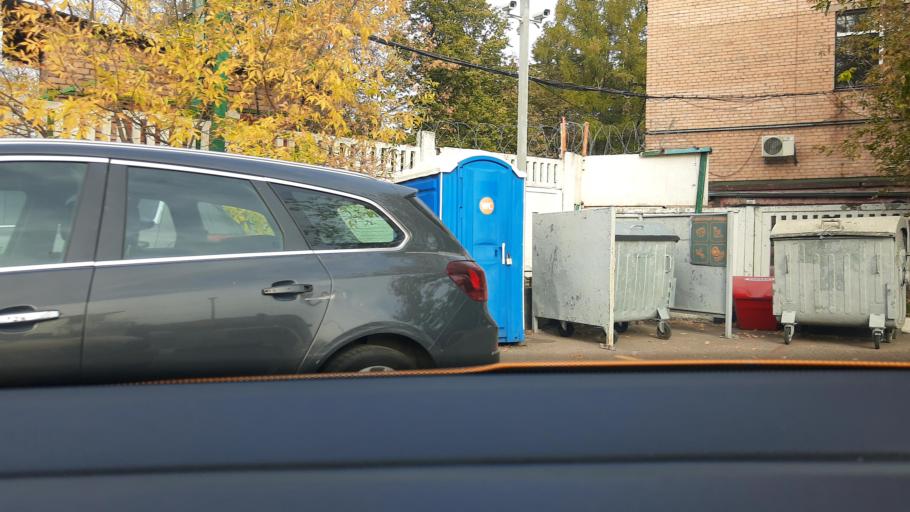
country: RU
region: Moskovskaya
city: Bogorodskoye
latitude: 55.7784
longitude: 37.7426
